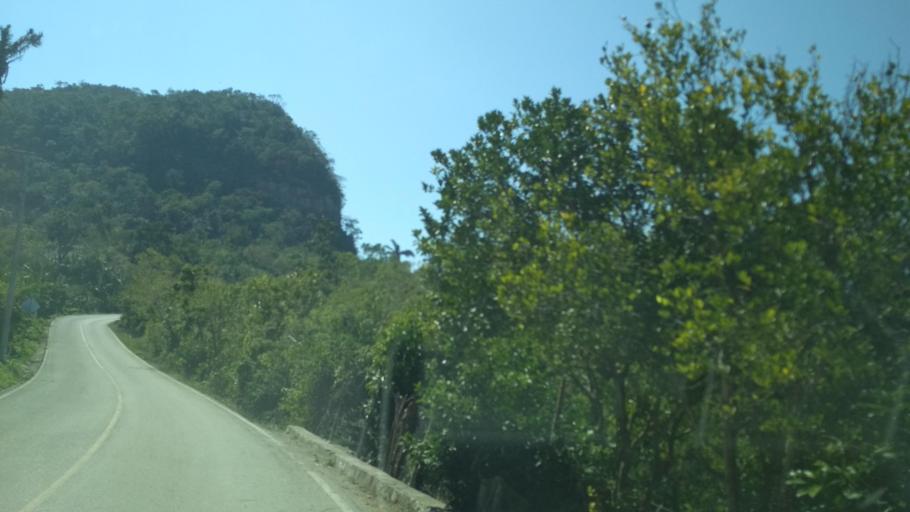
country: MX
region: Veracruz
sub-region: Papantla
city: Polutla
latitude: 20.4750
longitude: -97.2128
